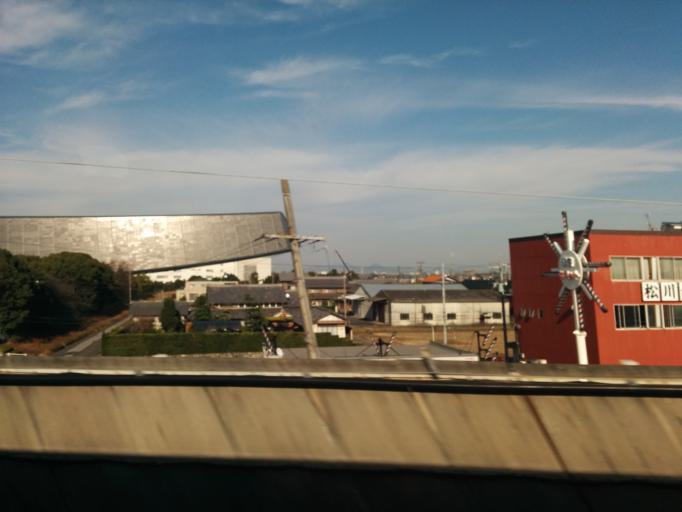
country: JP
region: Gifu
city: Ogaki
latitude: 35.3283
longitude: 136.6713
